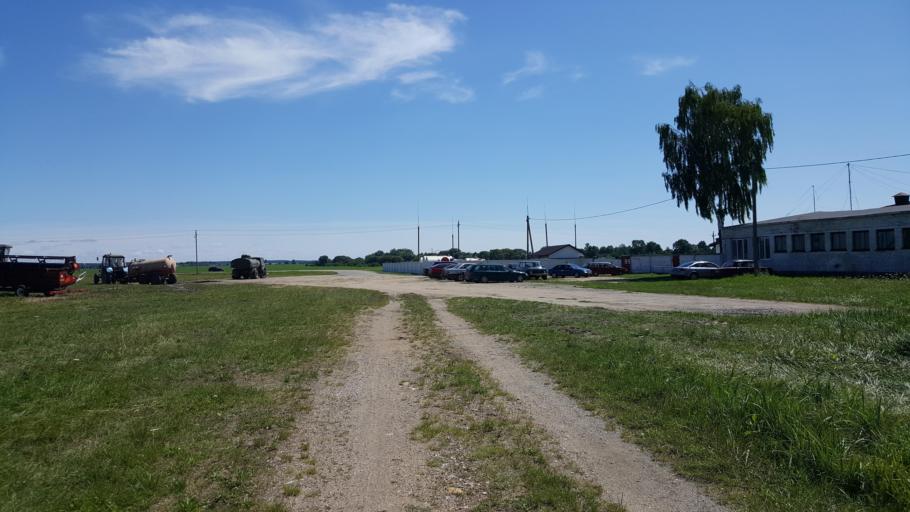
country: BY
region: Brest
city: Charnawchytsy
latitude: 52.2178
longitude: 23.7457
